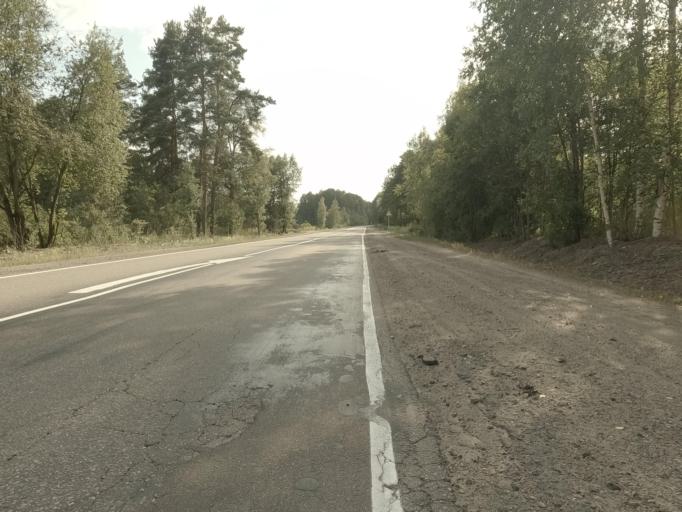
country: RU
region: Leningrad
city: Kamennogorsk
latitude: 60.8741
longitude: 28.9982
